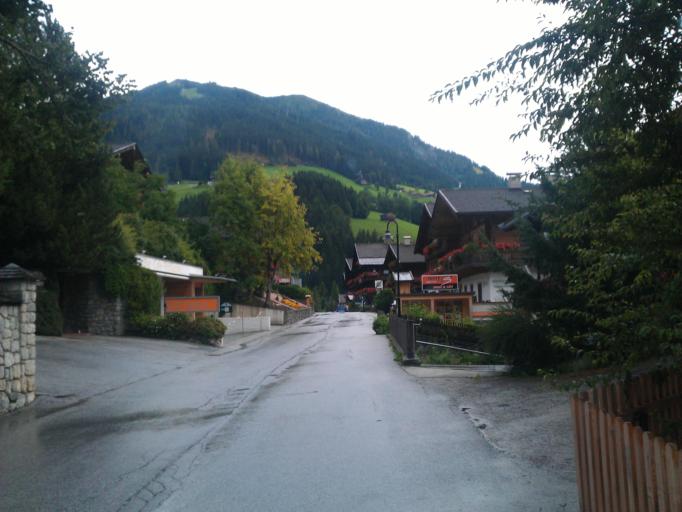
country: AT
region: Tyrol
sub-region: Politischer Bezirk Kufstein
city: Alpbach
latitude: 47.3981
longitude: 11.9445
